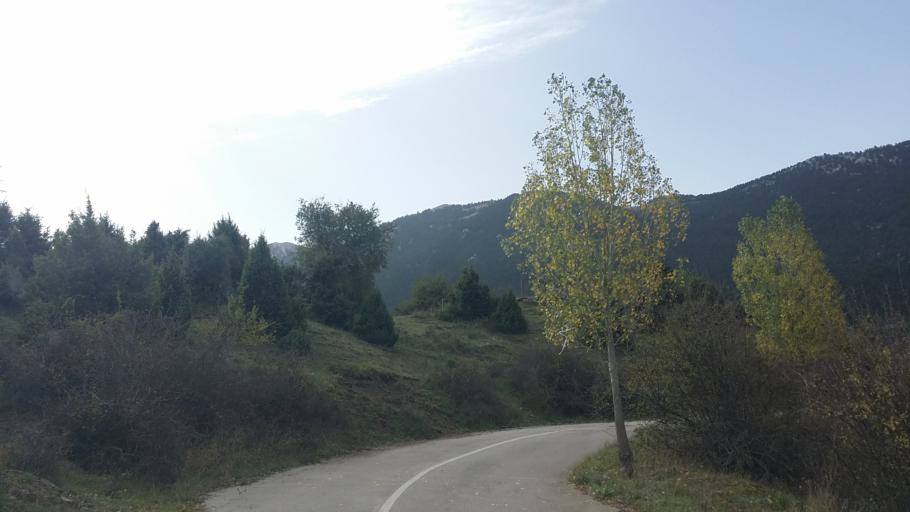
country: GR
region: Central Greece
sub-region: Nomos Voiotias
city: Kyriaki
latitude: 38.3694
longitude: 22.8454
